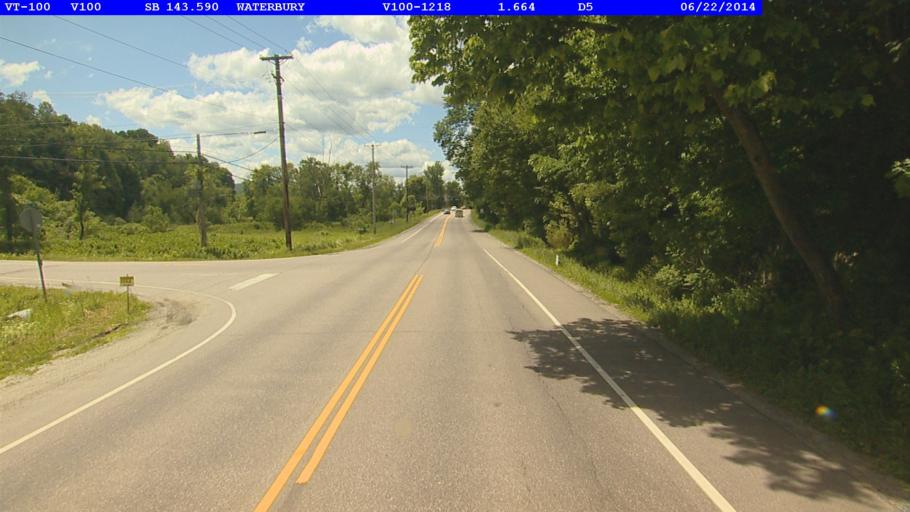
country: US
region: Vermont
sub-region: Washington County
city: Waterbury
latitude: 44.3559
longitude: -72.7357
